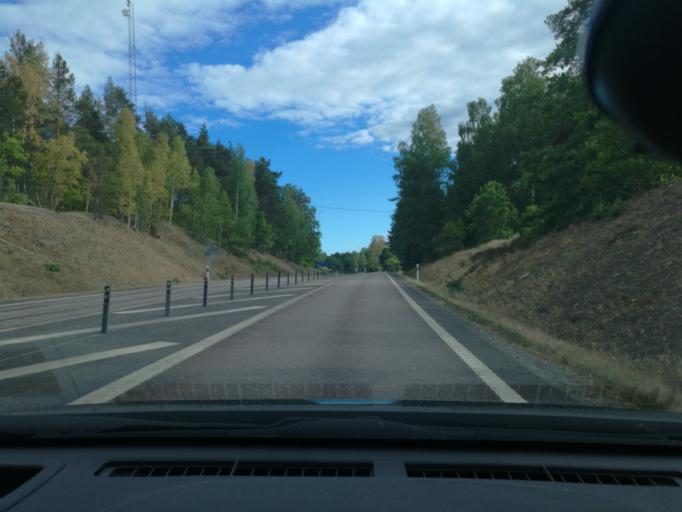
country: SE
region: Kalmar
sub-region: Oskarshamns Kommun
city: Oskarshamn
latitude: 57.4245
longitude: 16.4827
